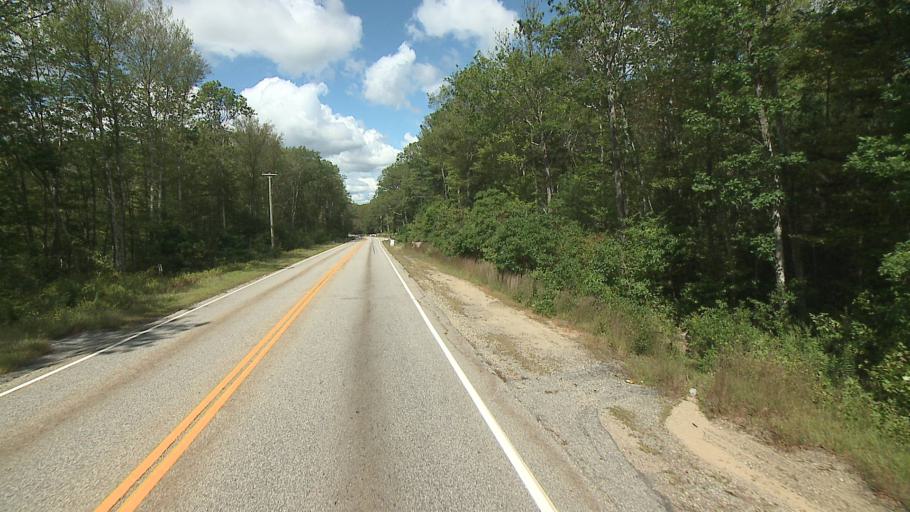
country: US
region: Connecticut
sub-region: Windham County
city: South Woodstock
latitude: 41.8667
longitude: -72.0490
